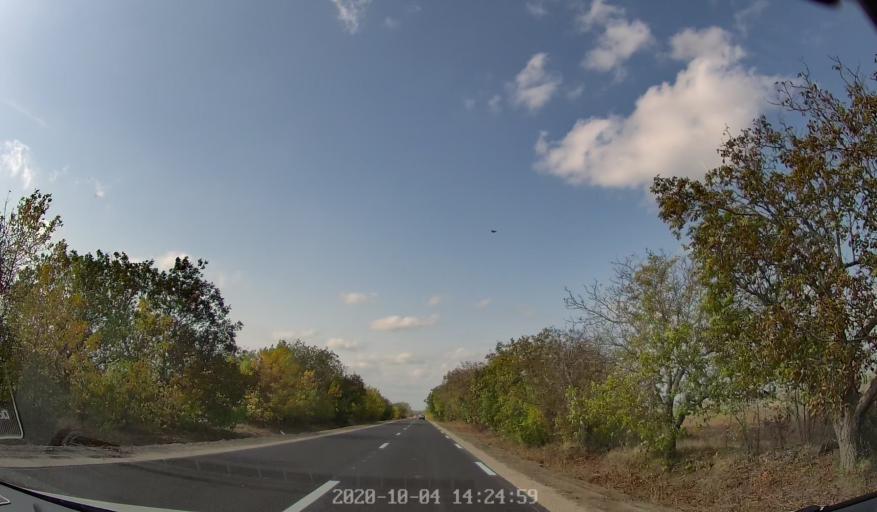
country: MD
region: Rezina
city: Saharna
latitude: 47.6172
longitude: 28.9065
